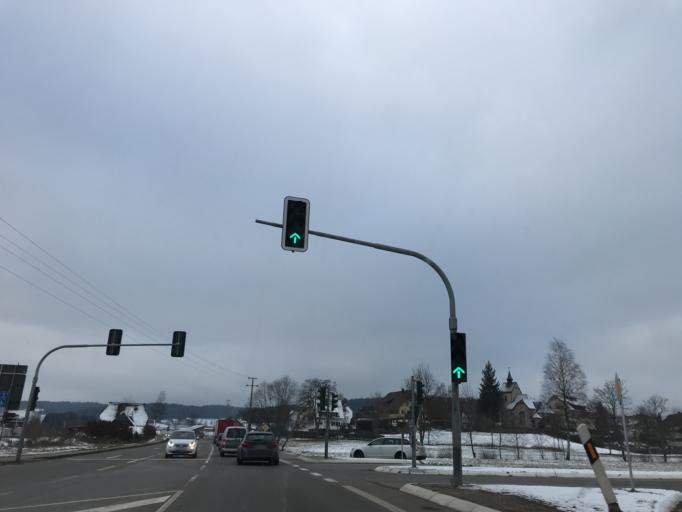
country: DE
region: Baden-Wuerttemberg
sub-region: Freiburg Region
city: Sankt Georgen im Schwarzwald
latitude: 48.1302
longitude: 8.3769
